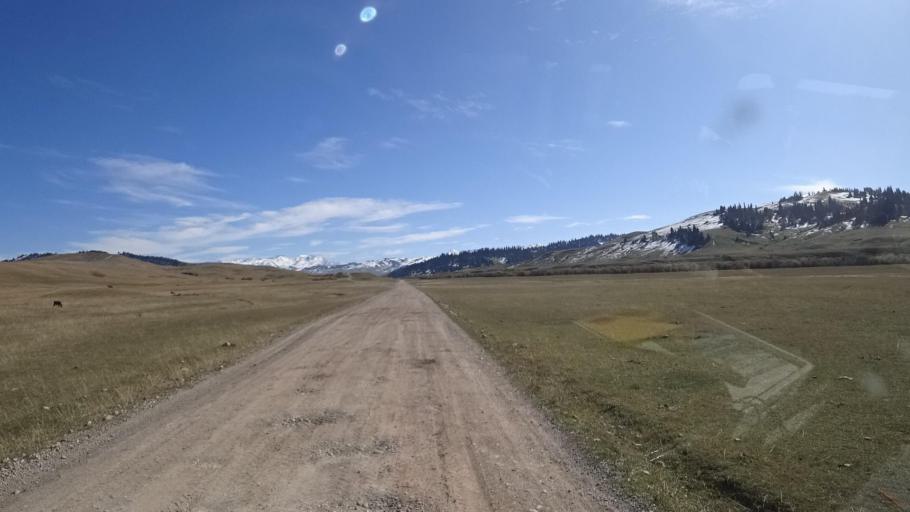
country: KZ
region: Almaty Oblysy
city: Kegen
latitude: 42.7415
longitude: 79.0024
